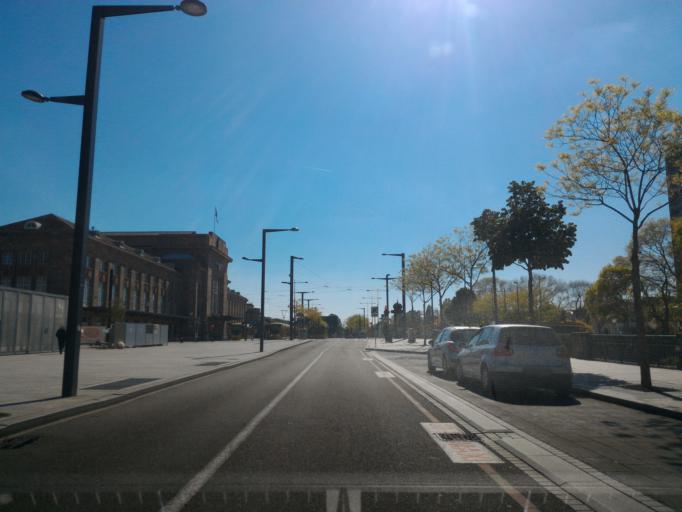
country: FR
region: Alsace
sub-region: Departement du Haut-Rhin
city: Mulhouse
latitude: 47.7437
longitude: 7.3443
